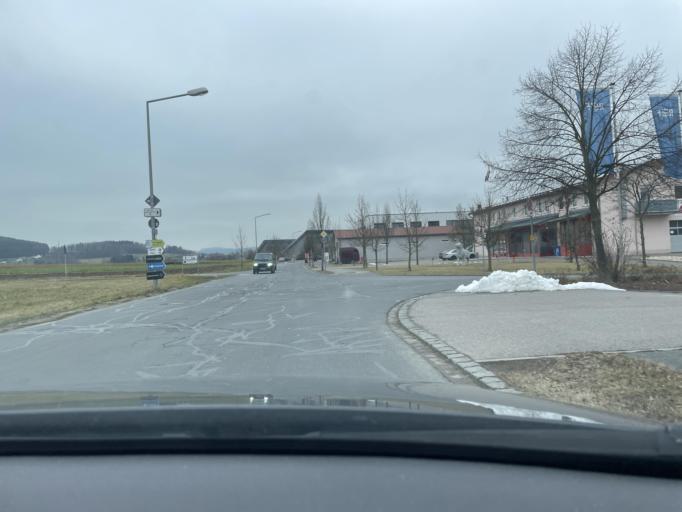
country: DE
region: Bavaria
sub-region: Upper Palatinate
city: Cham
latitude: 49.2076
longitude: 12.6817
